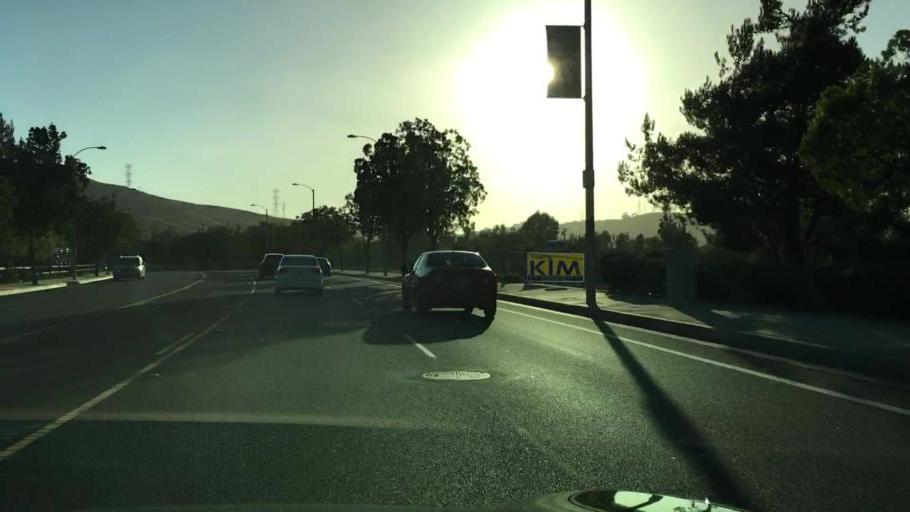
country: US
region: California
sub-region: Los Angeles County
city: Rowland Heights
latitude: 33.9745
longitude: -117.8919
